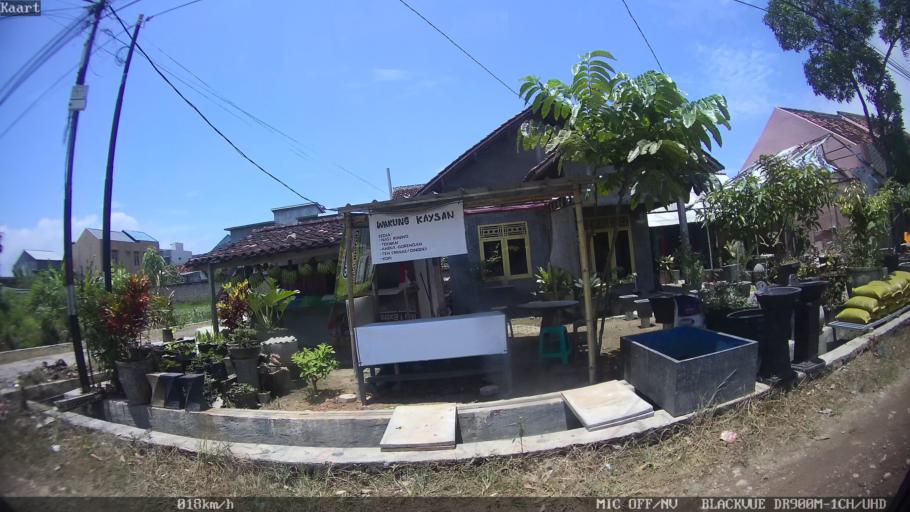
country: ID
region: Lampung
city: Kedaton
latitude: -5.3725
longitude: 105.2887
